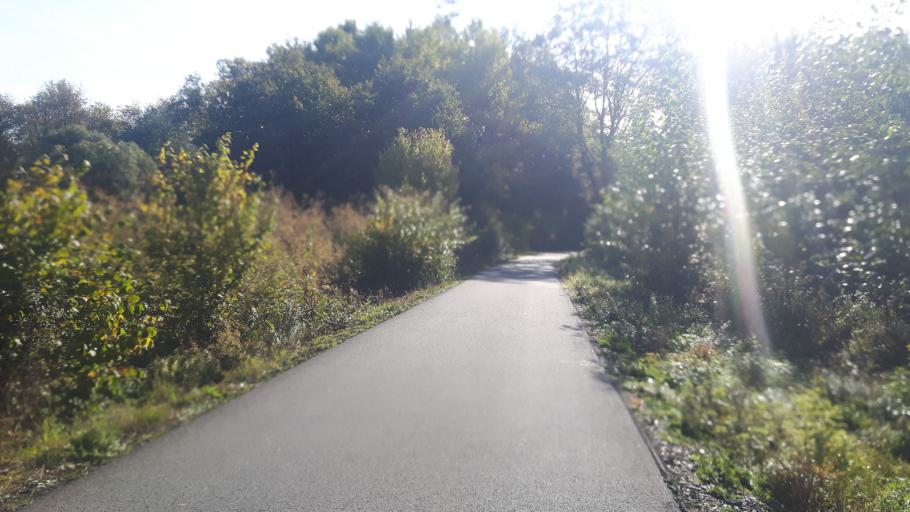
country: DE
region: North Rhine-Westphalia
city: Netphen
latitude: 50.8938
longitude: 8.1200
